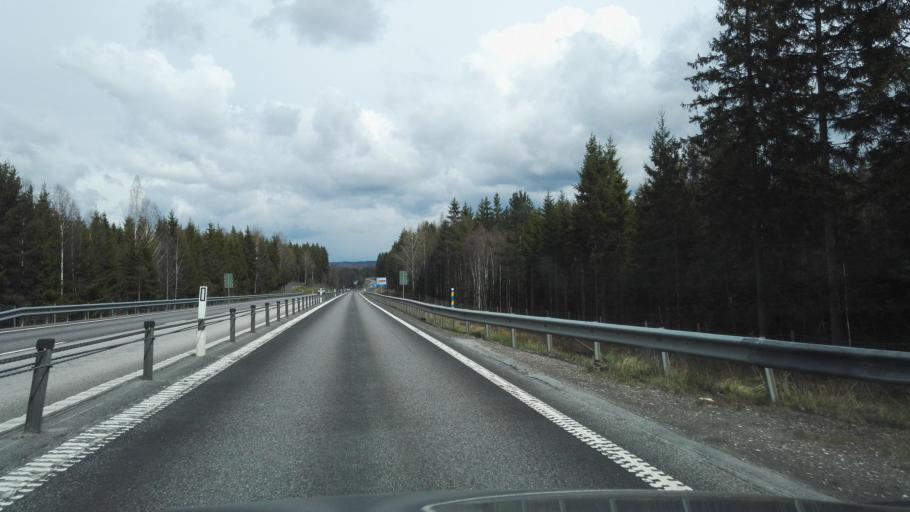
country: SE
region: Kronoberg
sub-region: Vaxjo Kommun
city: Rottne
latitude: 56.9629
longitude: 14.9548
